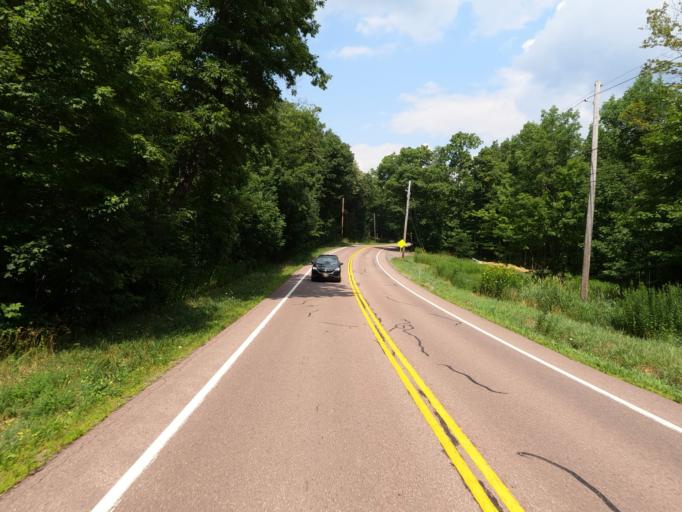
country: US
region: Maryland
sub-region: Allegany County
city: Westernport
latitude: 39.6419
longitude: -79.2018
